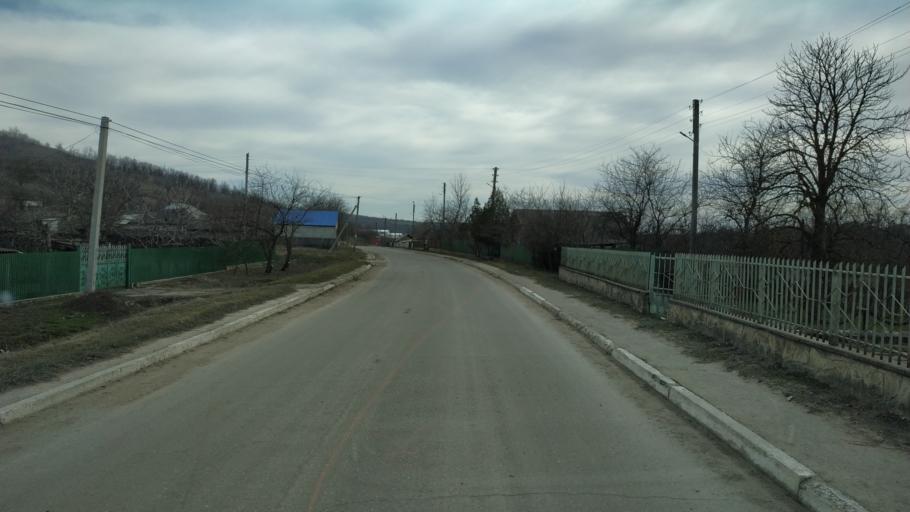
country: MD
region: Nisporeni
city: Nisporeni
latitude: 46.9652
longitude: 28.2147
